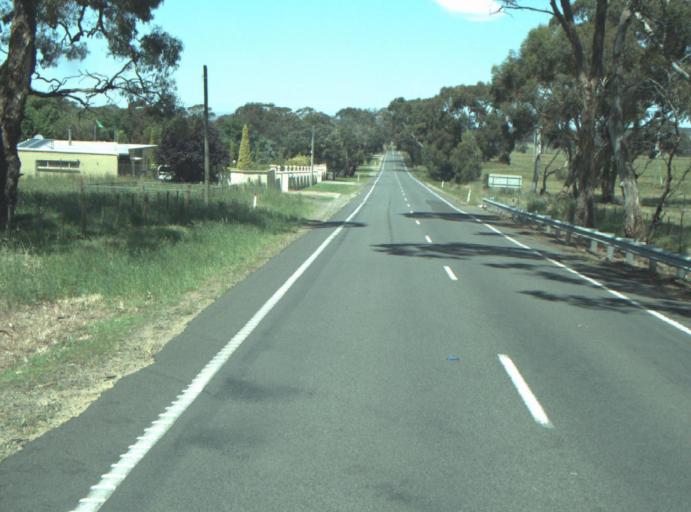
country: AU
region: Victoria
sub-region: Greater Geelong
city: Lara
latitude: -37.8890
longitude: 144.2567
